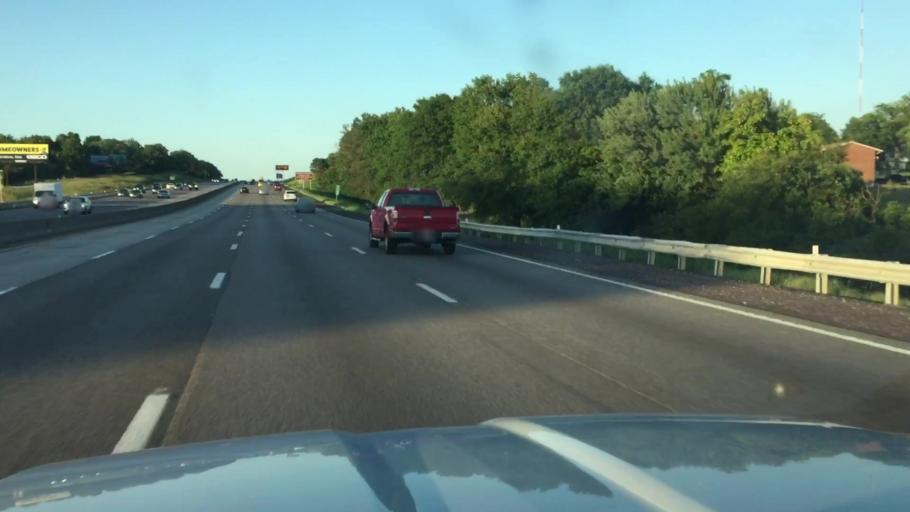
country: US
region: Missouri
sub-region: Saint Louis County
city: Saint George
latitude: 38.5250
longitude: -90.3193
